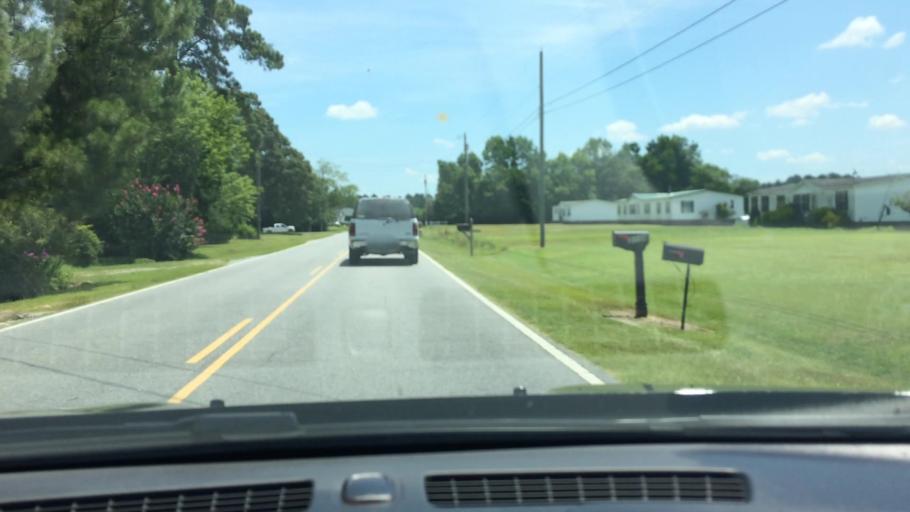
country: US
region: North Carolina
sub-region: Pitt County
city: Windsor
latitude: 35.5468
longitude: -77.2698
